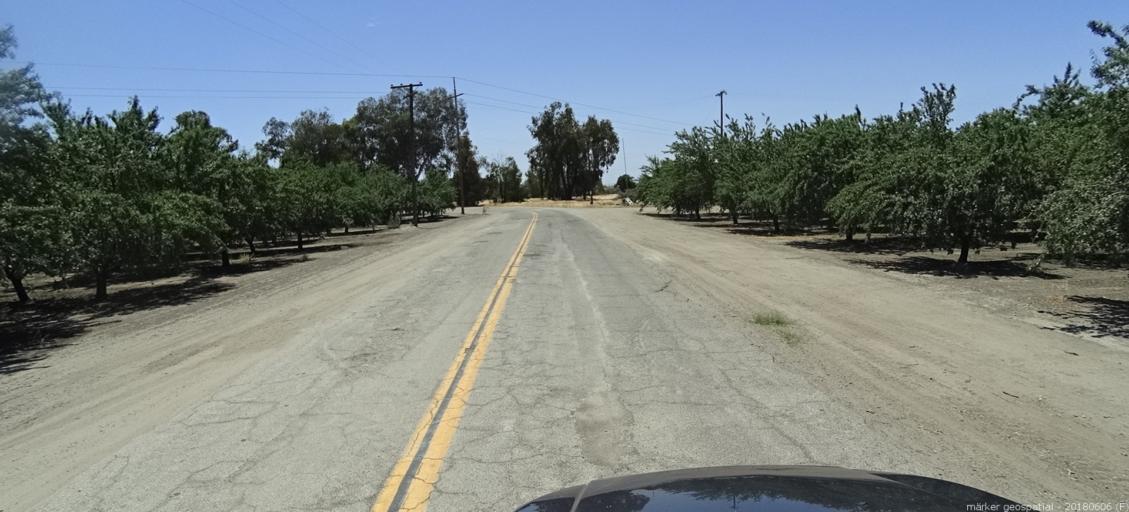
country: US
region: California
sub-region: Fresno County
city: Firebaugh
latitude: 36.8439
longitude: -120.4179
